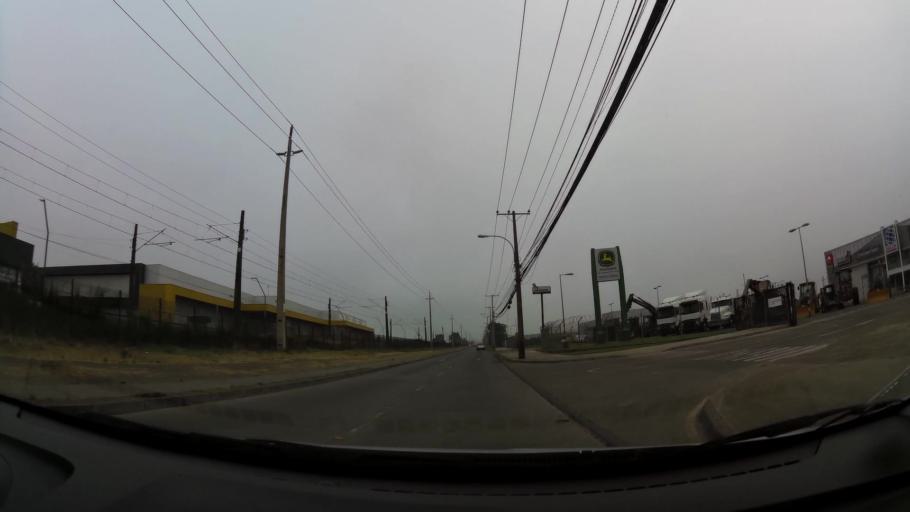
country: CL
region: Biobio
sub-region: Provincia de Concepcion
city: Concepcion
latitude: -36.8027
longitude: -73.0781
